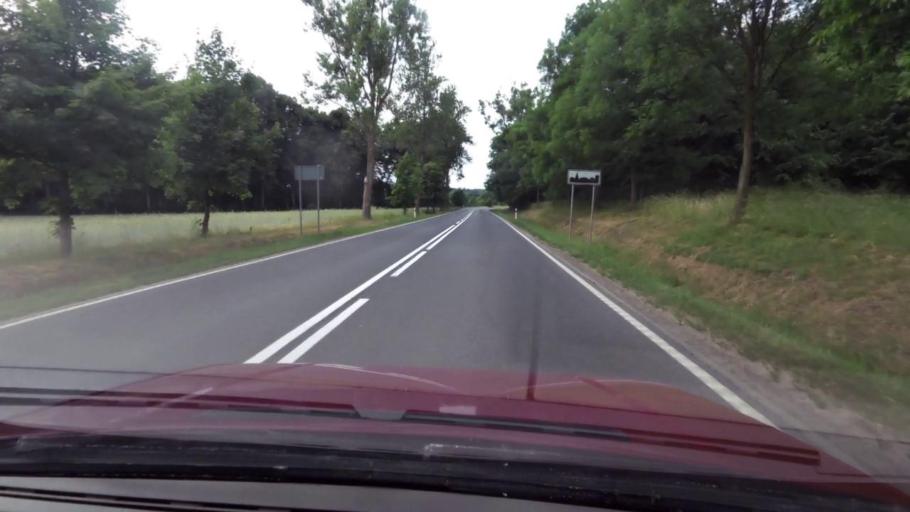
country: PL
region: Pomeranian Voivodeship
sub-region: Powiat bytowski
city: Trzebielino
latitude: 54.2704
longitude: 17.0981
